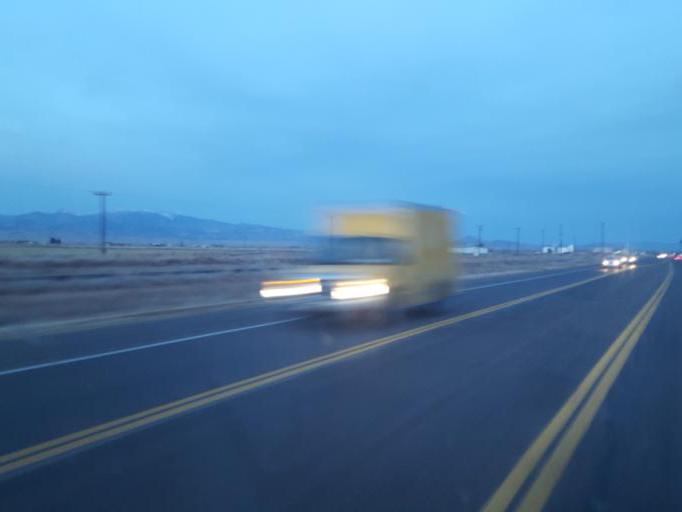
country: US
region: Colorado
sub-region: Rio Grande County
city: Monte Vista
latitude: 37.5573
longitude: -106.0886
